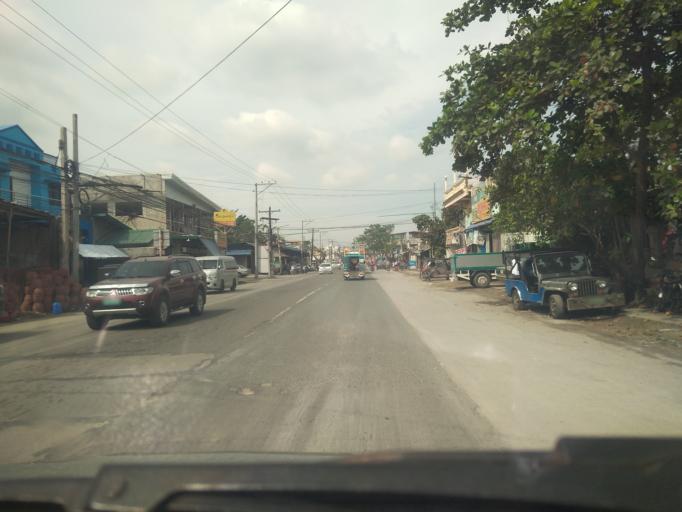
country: PH
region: Central Luzon
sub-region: Province of Pampanga
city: Pau
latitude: 15.0067
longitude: 120.7147
